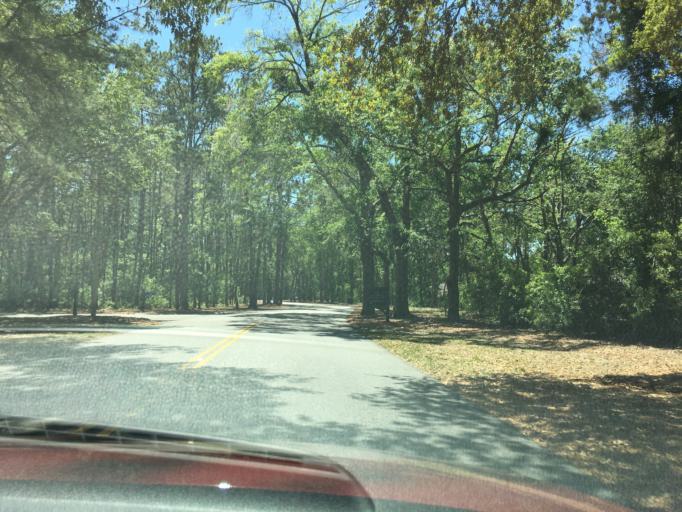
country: US
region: South Carolina
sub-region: Beaufort County
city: Hilton Head Island
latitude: 32.2011
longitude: -80.7293
